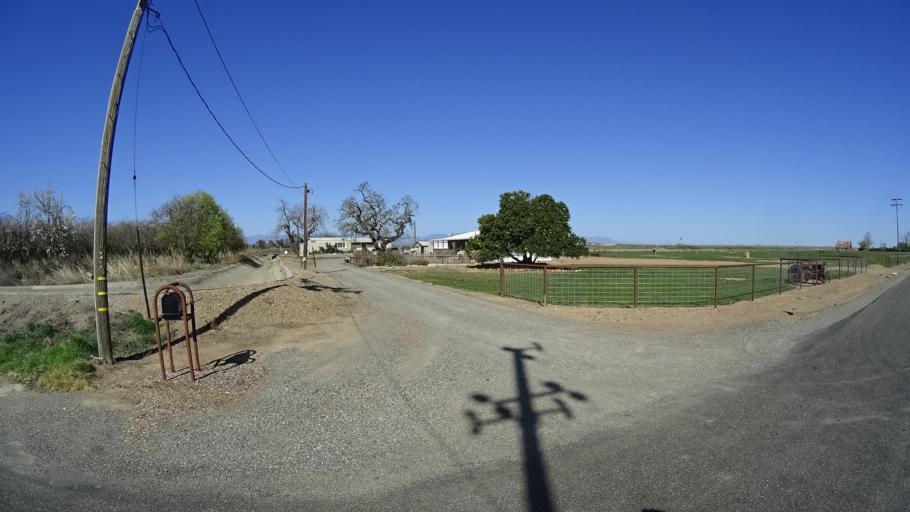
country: US
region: California
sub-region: Glenn County
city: Orland
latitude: 39.7441
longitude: -122.2480
